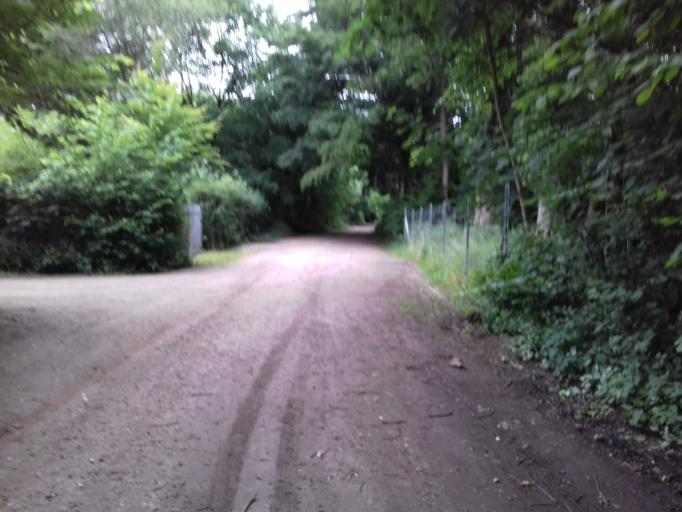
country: DE
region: Schleswig-Holstein
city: Tasdorf
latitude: 54.0839
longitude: 10.0103
